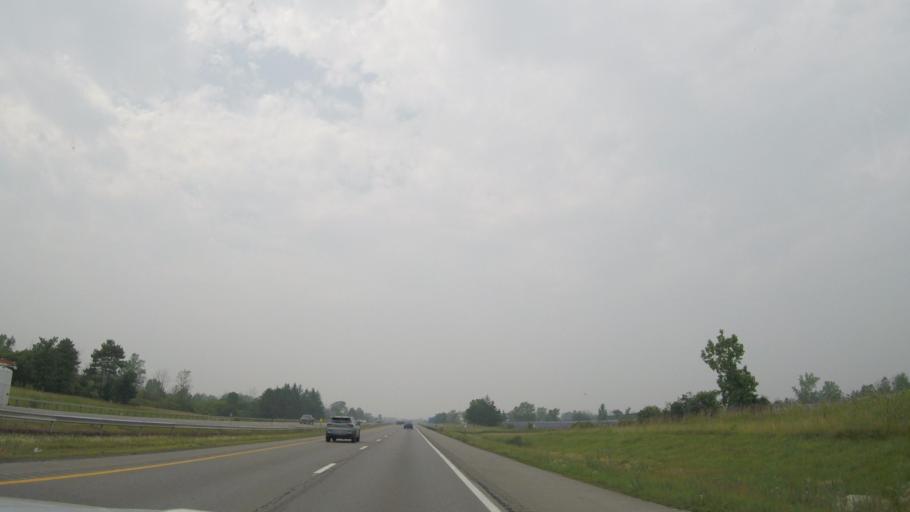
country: US
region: New York
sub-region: Erie County
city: Grandyle Village
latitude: 43.0364
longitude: -78.9842
